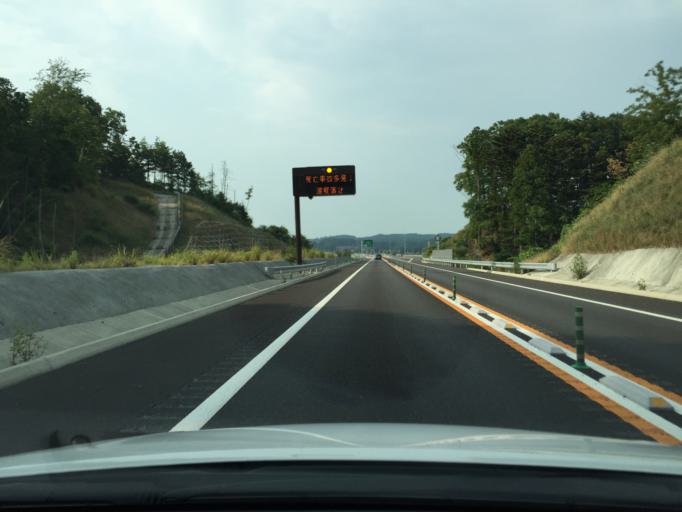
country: JP
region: Fukushima
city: Namie
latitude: 37.6534
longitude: 140.9184
